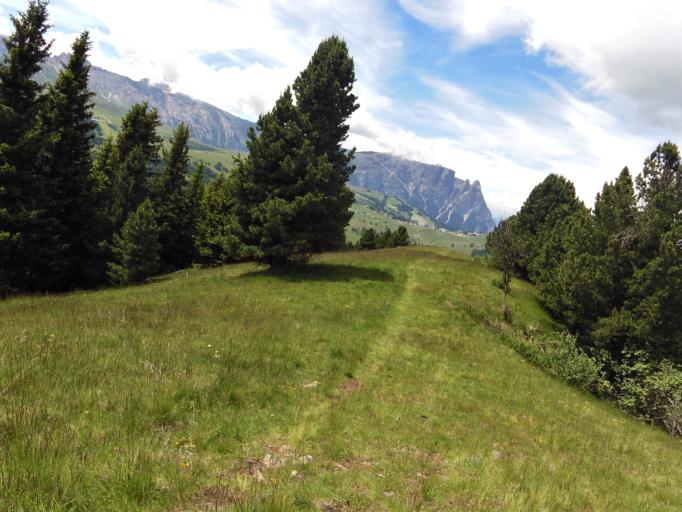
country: IT
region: Trentino-Alto Adige
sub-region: Bolzano
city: Ortisei
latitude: 46.5573
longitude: 11.6516
